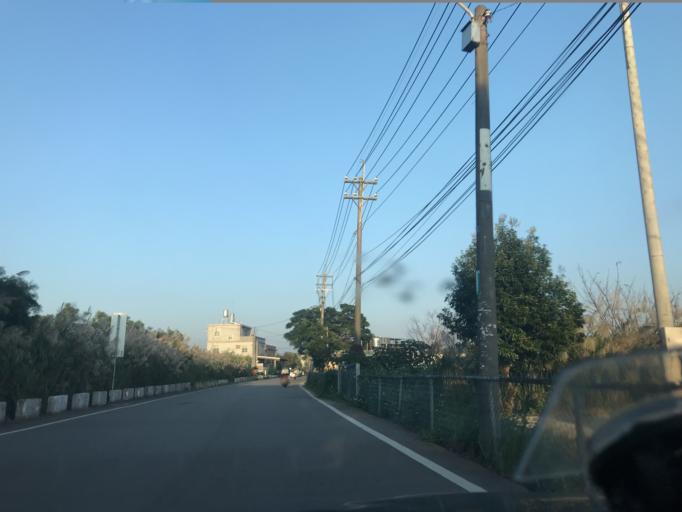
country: TW
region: Taiwan
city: Daxi
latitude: 24.8455
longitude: 121.2229
